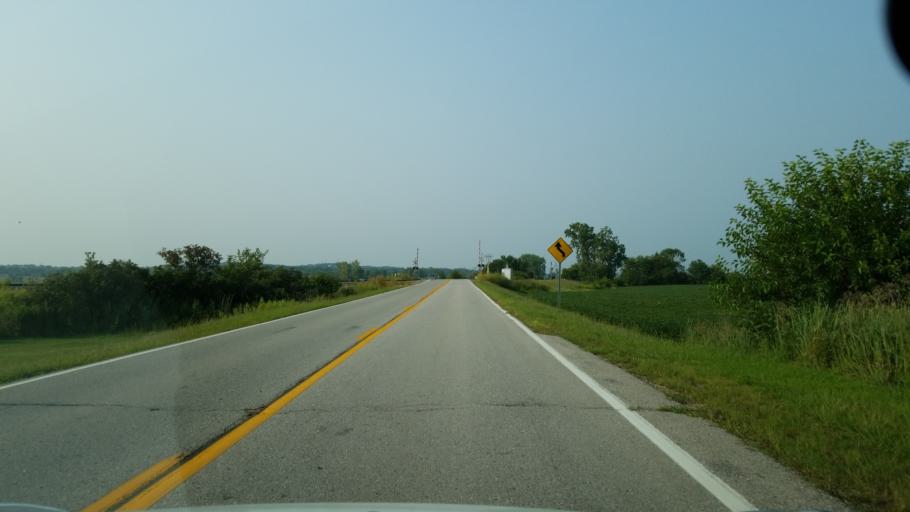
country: US
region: Nebraska
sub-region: Sarpy County
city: Bellevue
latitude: 41.1089
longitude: -95.8899
